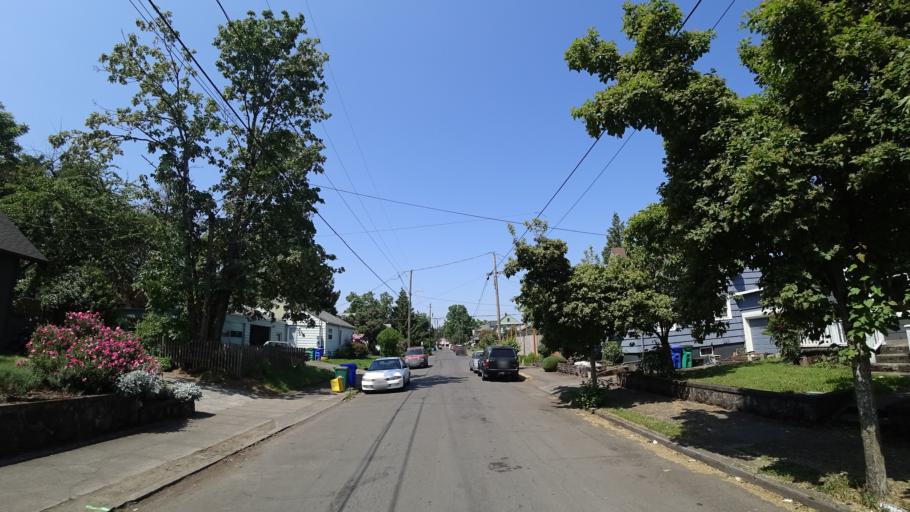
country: US
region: Oregon
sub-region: Multnomah County
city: Portland
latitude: 45.5641
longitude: -122.6581
